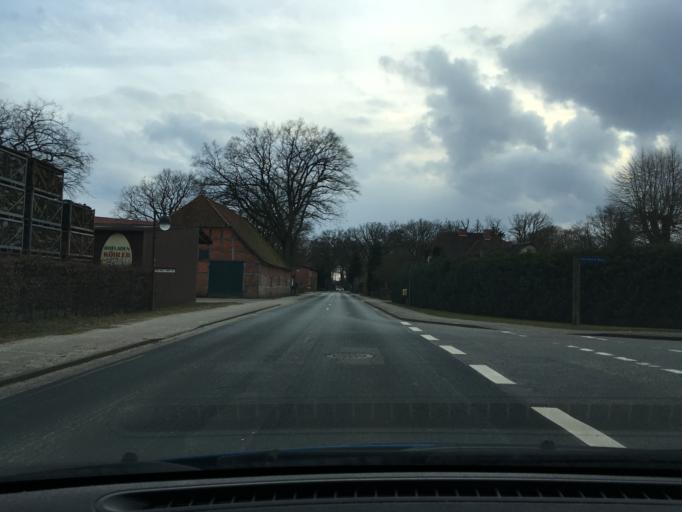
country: DE
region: Lower Saxony
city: Kirchgellersen
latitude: 53.2542
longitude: 10.3196
